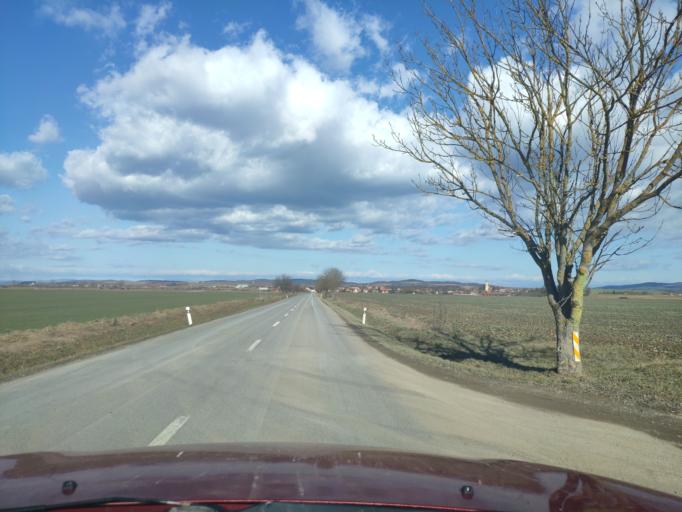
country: HU
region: Borsod-Abauj-Zemplen
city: Ozd
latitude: 48.3106
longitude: 20.3229
